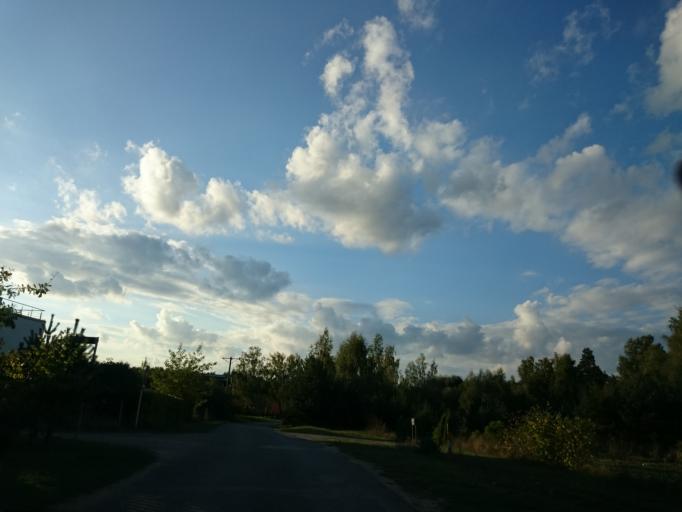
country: LV
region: Adazi
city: Adazi
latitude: 57.0662
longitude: 24.2736
